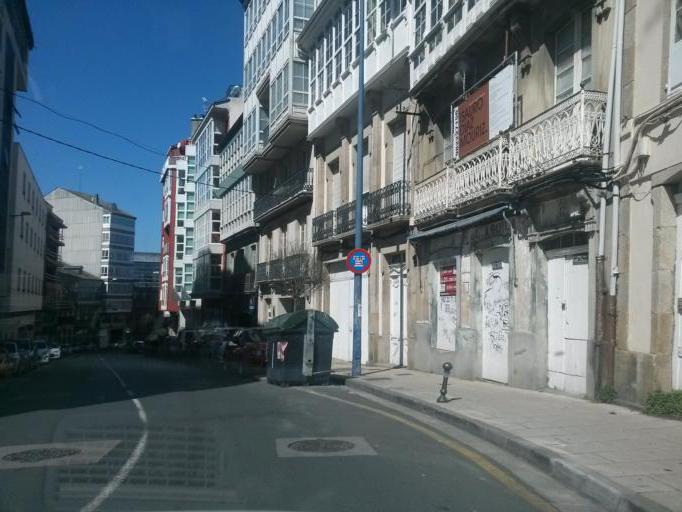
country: ES
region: Galicia
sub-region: Provincia de Lugo
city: Lugo
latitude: 43.0132
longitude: -7.5544
